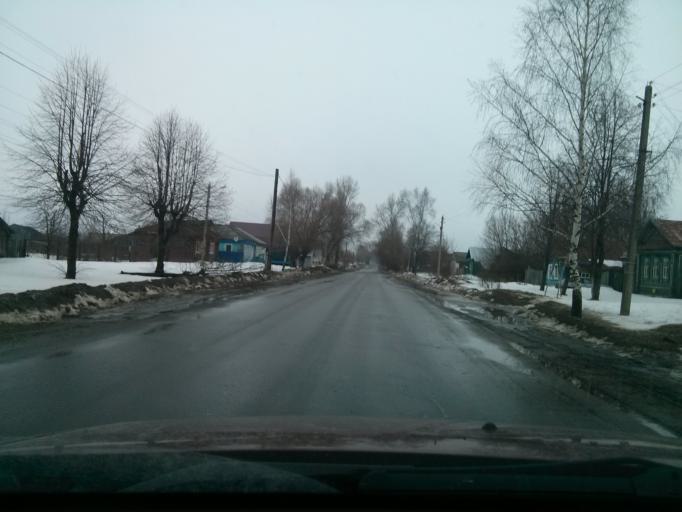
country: RU
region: Vladimir
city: Murom
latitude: 55.5352
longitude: 42.0243
